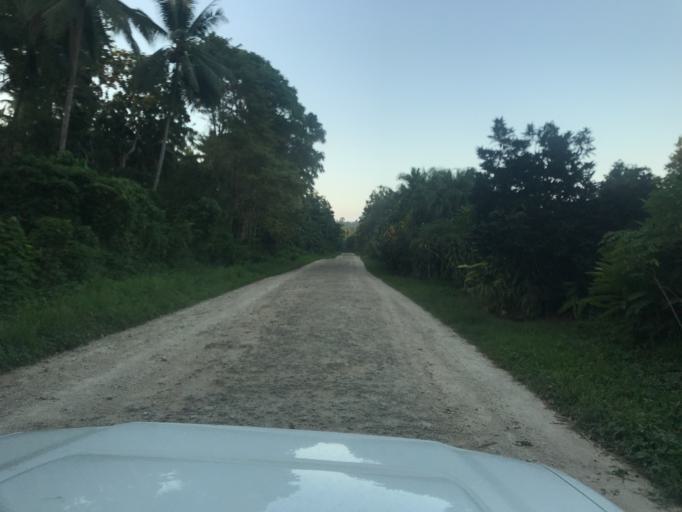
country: VU
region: Sanma
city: Luganville
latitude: -15.5666
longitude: 166.9582
